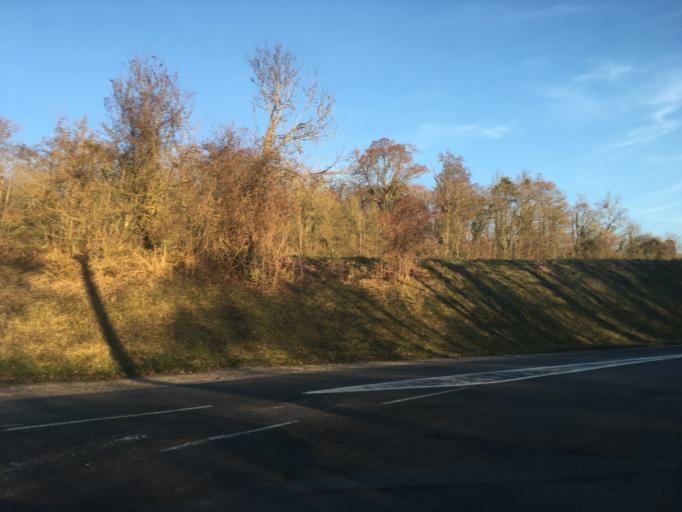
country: FR
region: Haute-Normandie
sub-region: Departement de l'Eure
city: Houlbec-Cocherel
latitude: 49.0591
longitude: 1.3335
